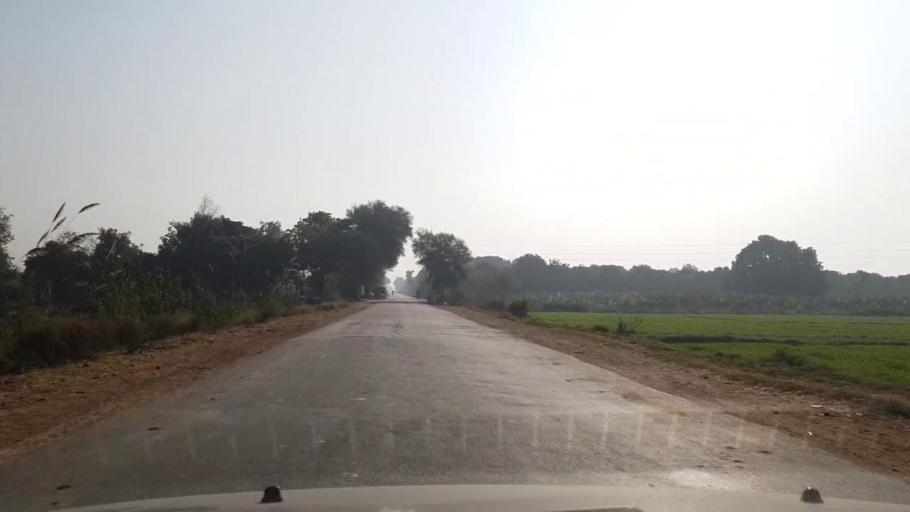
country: PK
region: Sindh
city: Matiari
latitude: 25.5978
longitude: 68.4596
